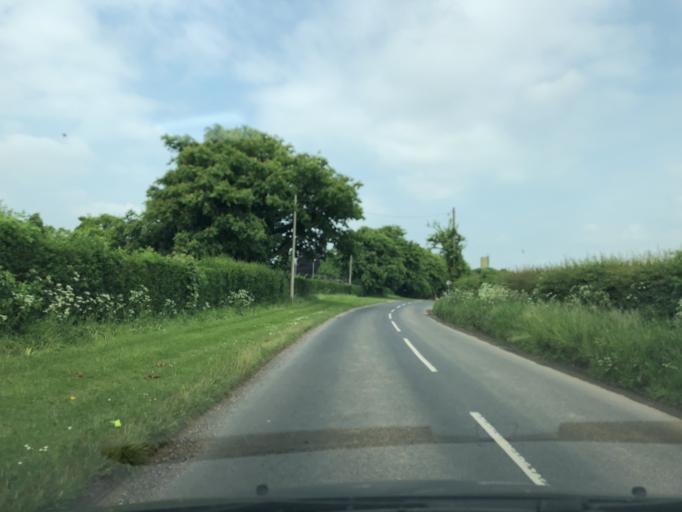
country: GB
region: England
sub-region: North Yorkshire
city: Boroughbridge
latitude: 54.1356
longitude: -1.4074
